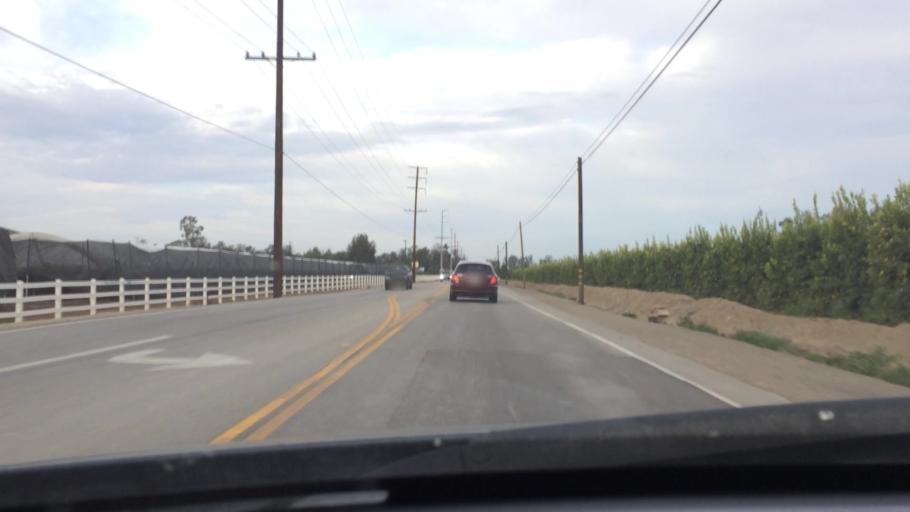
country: US
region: California
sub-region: Ventura County
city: Camarillo
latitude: 34.2639
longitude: -119.0350
